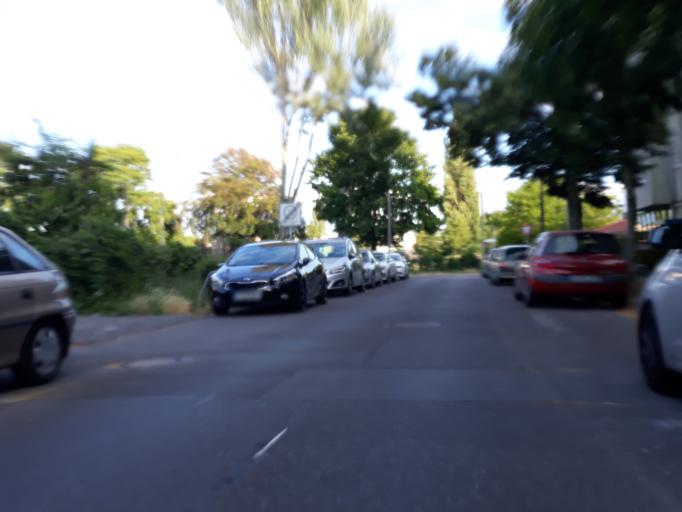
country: DE
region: Berlin
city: Adlershof
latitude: 52.4409
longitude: 13.5547
